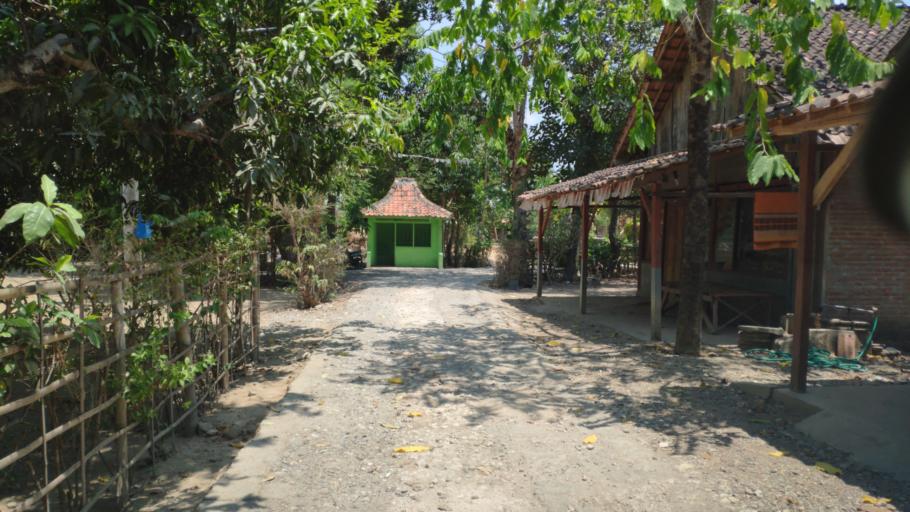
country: ID
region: Central Java
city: Nglaroh
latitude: -6.9573
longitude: 111.4486
